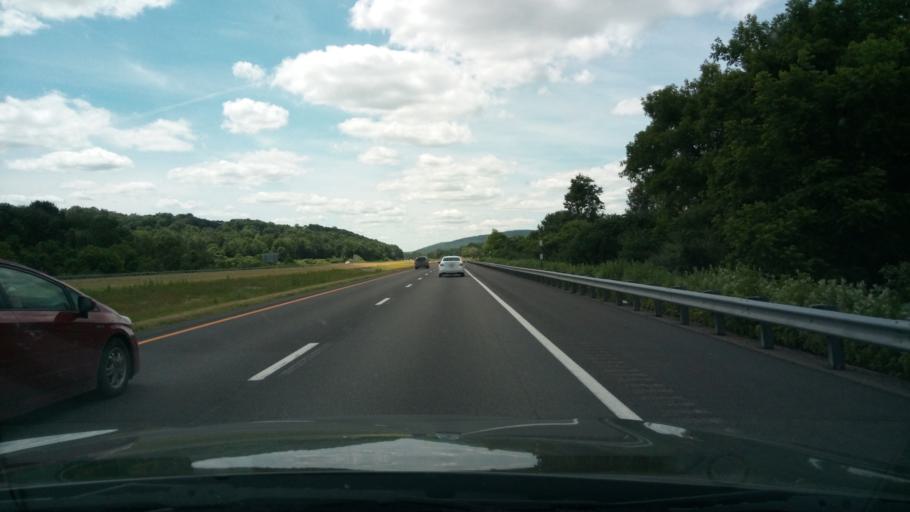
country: US
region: Pennsylvania
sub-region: Bradford County
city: South Waverly
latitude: 42.0165
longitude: -76.6434
